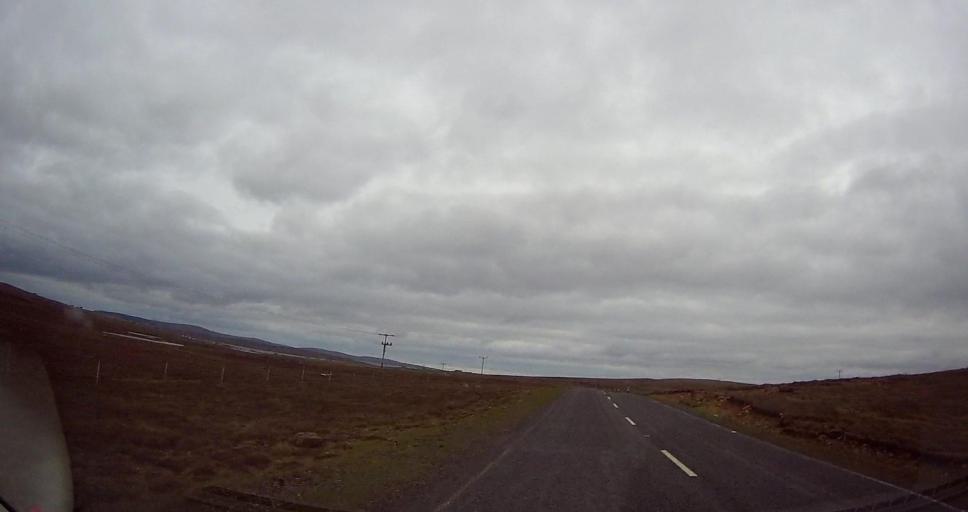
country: GB
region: Scotland
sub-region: Shetland Islands
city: Shetland
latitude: 60.7115
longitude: -0.9172
